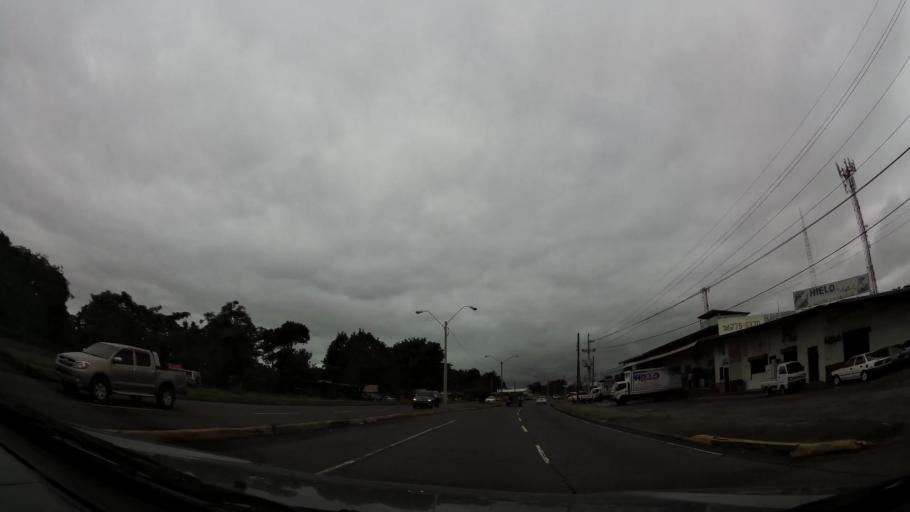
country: PA
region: Chiriqui
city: David
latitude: 8.4290
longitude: -82.4447
